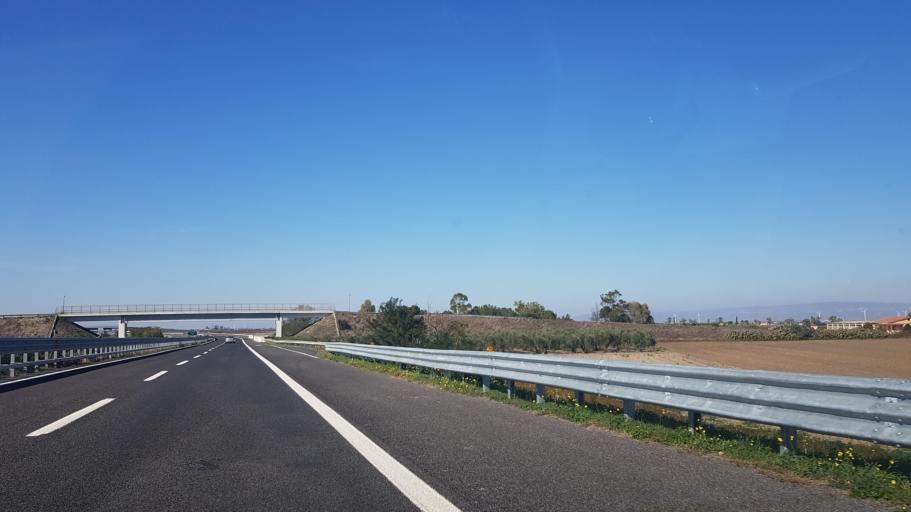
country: IT
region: Apulia
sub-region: Provincia di Foggia
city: Carapelle
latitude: 41.3820
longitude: 15.7509
